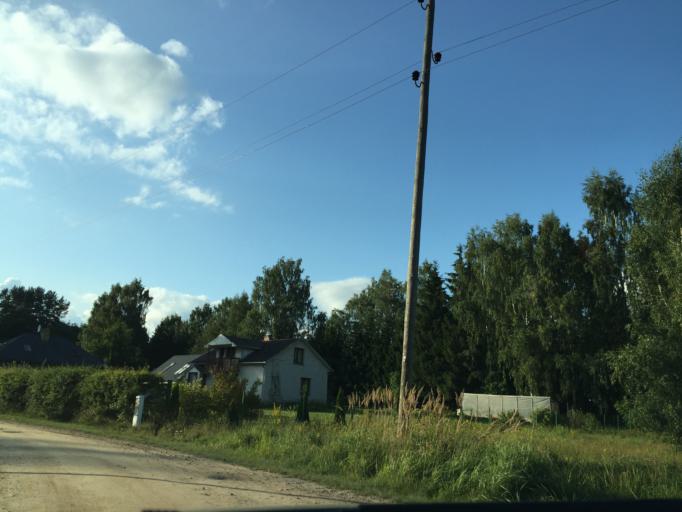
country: LV
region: Ikskile
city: Ikskile
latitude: 56.8372
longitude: 24.5123
